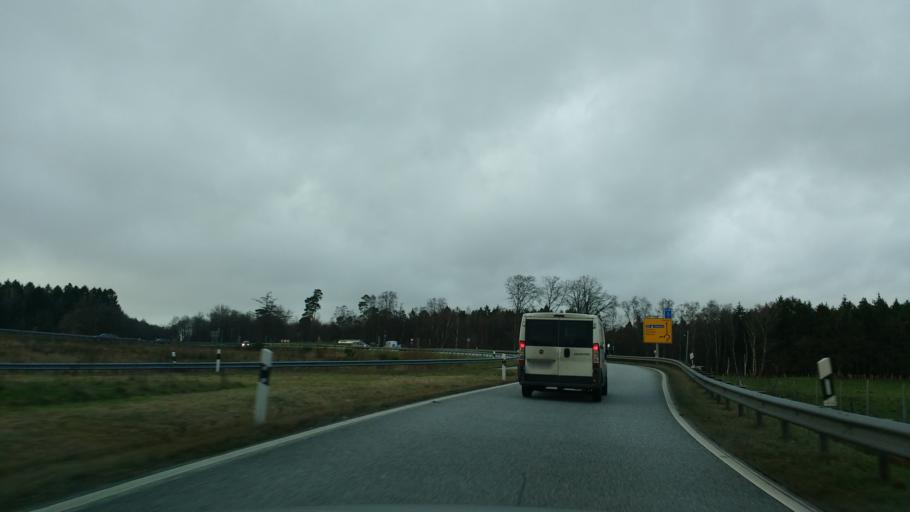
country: DE
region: Schleswig-Holstein
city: Dageling
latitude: 53.8957
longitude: 9.5163
